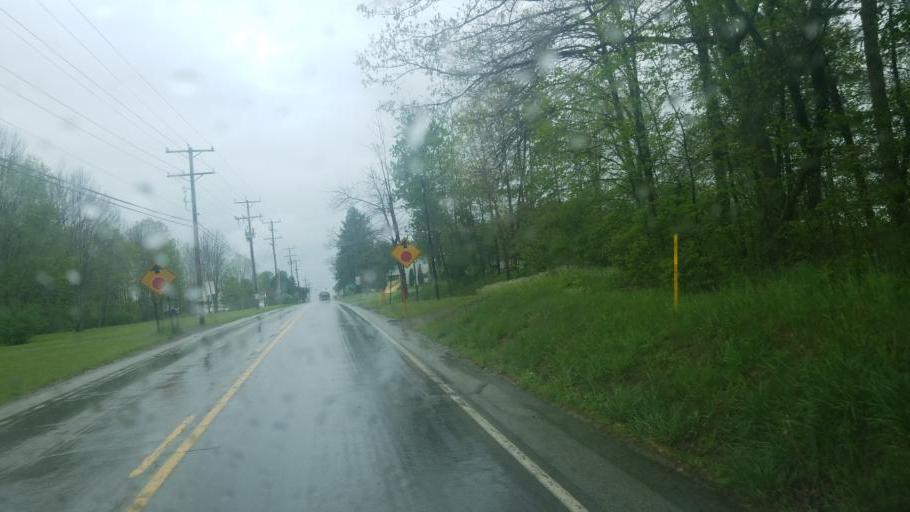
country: US
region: Pennsylvania
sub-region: Forest County
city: Tionesta
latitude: 41.3954
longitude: -79.3648
